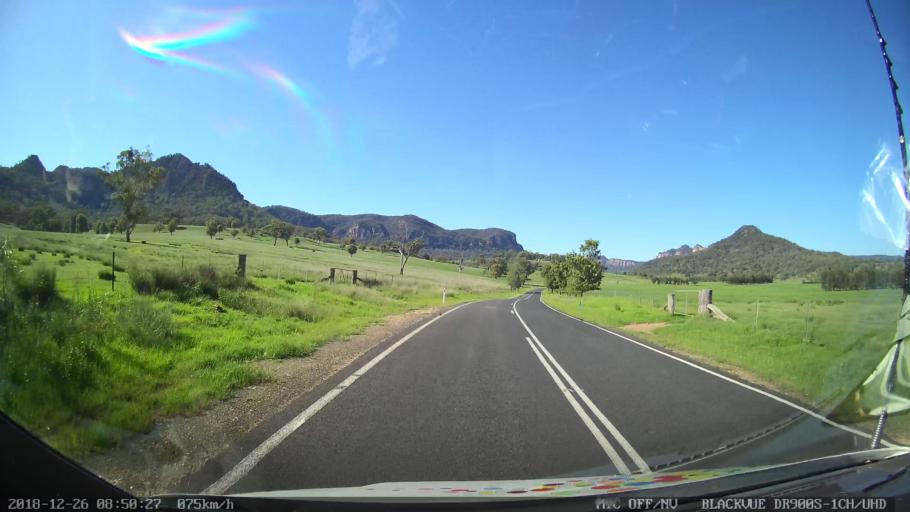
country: AU
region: New South Wales
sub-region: Mid-Western Regional
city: Kandos
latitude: -32.5755
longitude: 150.0949
